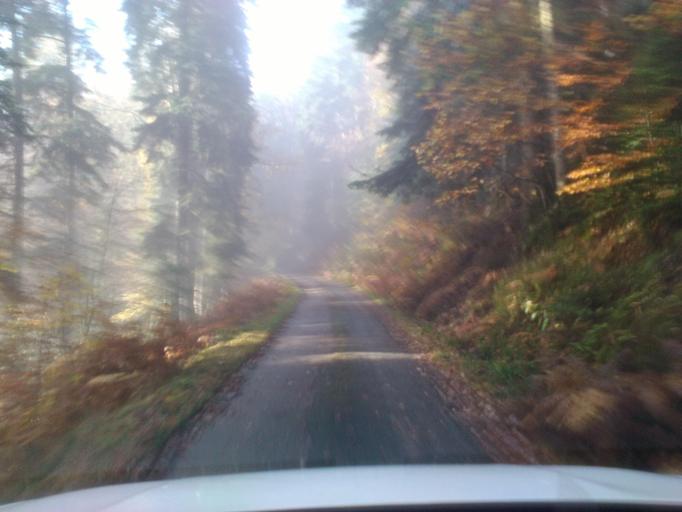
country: FR
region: Lorraine
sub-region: Departement des Vosges
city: Senones
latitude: 48.4107
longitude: 6.9738
